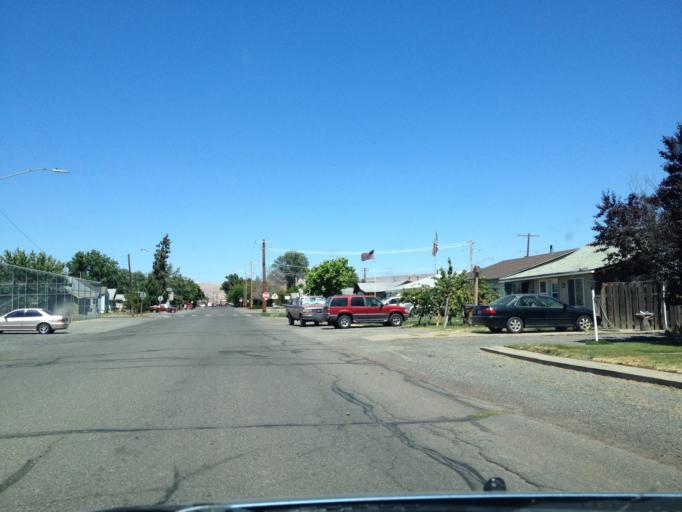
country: US
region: Washington
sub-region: Yakima County
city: Union Gap
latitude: 46.5551
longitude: -120.4778
